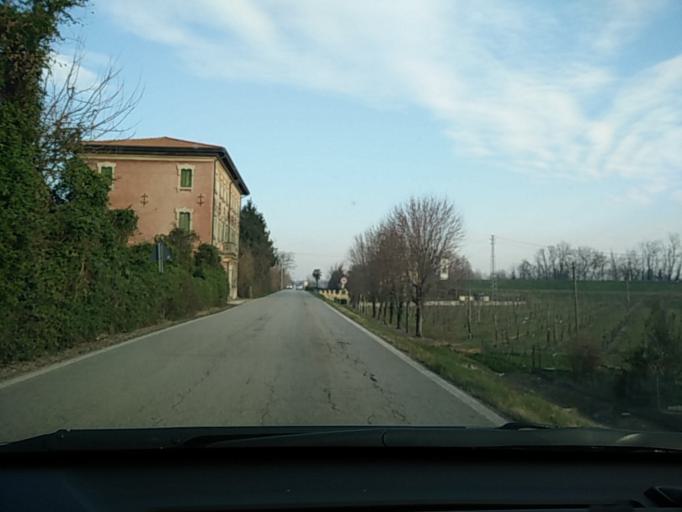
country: IT
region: Veneto
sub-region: Provincia di Venezia
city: Fossalta di Piave
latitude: 45.6492
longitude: 12.5126
